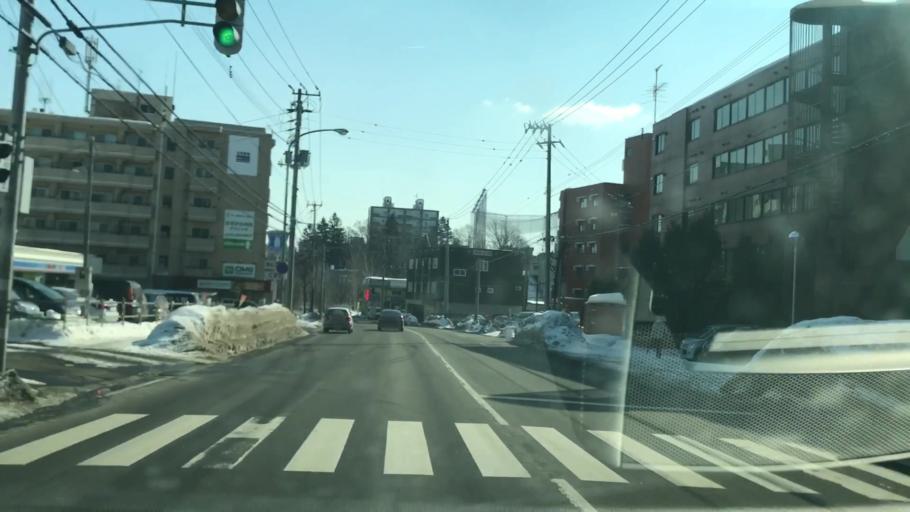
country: JP
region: Hokkaido
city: Sapporo
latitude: 43.0242
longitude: 141.3831
